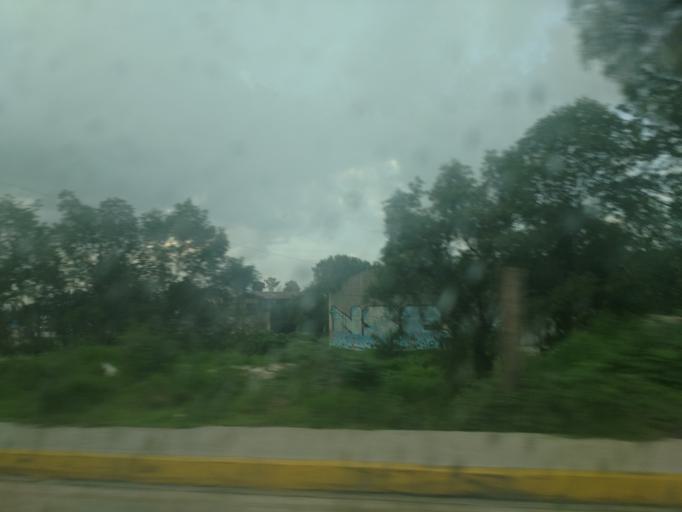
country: MX
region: Morelos
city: Coyotepec
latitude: 19.7831
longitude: -99.2208
